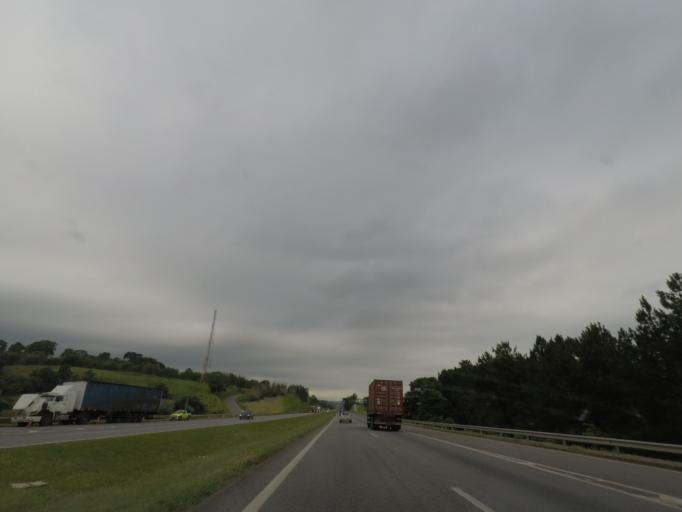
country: BR
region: Sao Paulo
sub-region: Jarinu
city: Jarinu
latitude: -23.0718
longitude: -46.6408
